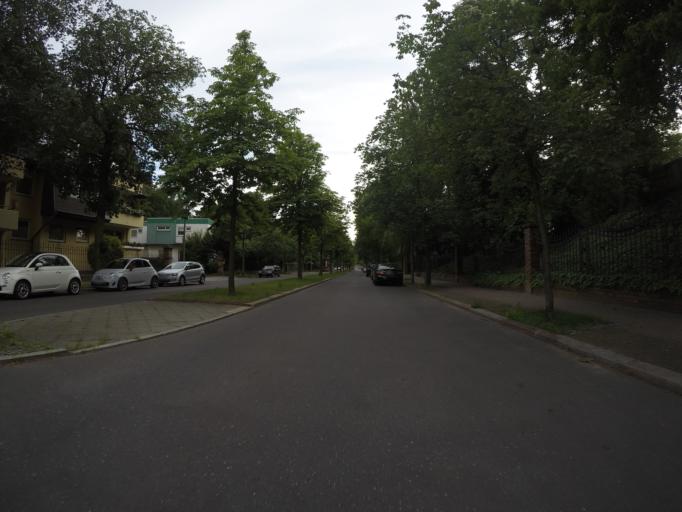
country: DE
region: Berlin
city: Halensee
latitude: 52.4896
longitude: 13.2809
